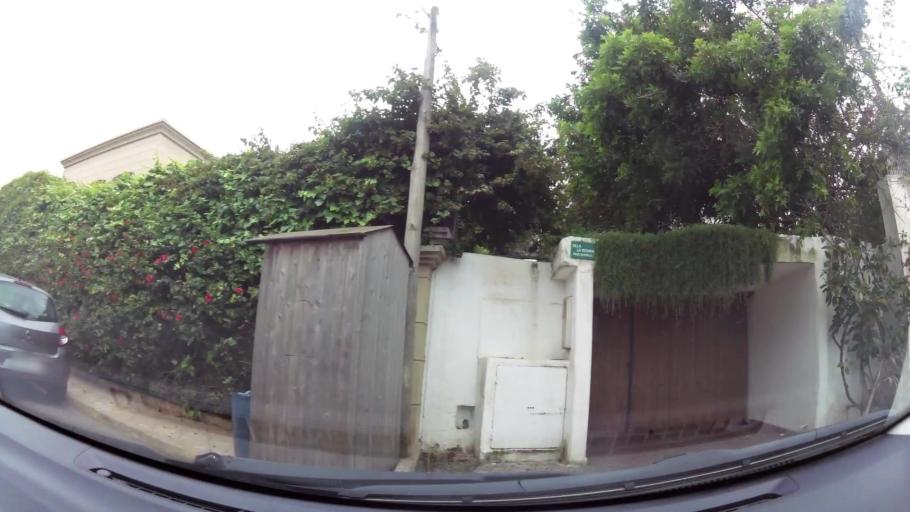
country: MA
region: Grand Casablanca
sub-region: Casablanca
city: Casablanca
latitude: 33.5996
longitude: -7.6620
